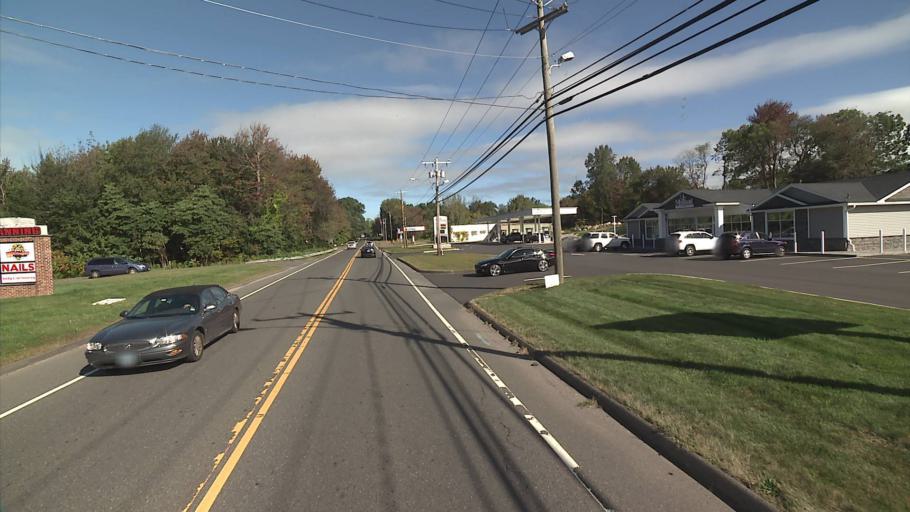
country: US
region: Connecticut
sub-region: New Haven County
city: Wolcott
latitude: 41.6295
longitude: -72.9617
